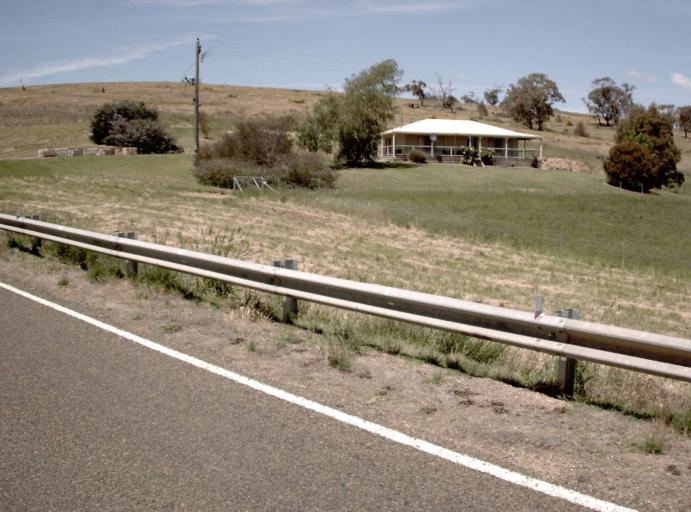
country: AU
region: Victoria
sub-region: Alpine
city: Mount Beauty
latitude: -37.1068
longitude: 147.6031
